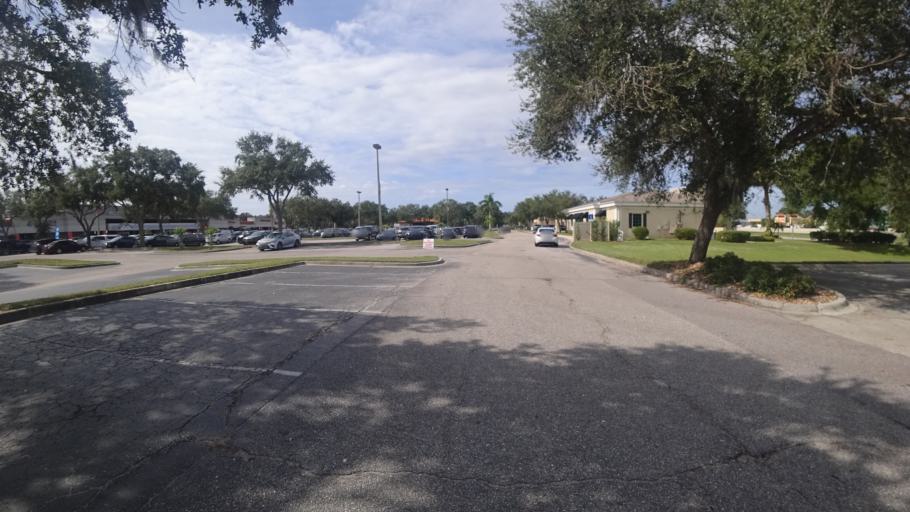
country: US
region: Florida
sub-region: Sarasota County
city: North Sarasota
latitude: 27.3879
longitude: -82.5033
